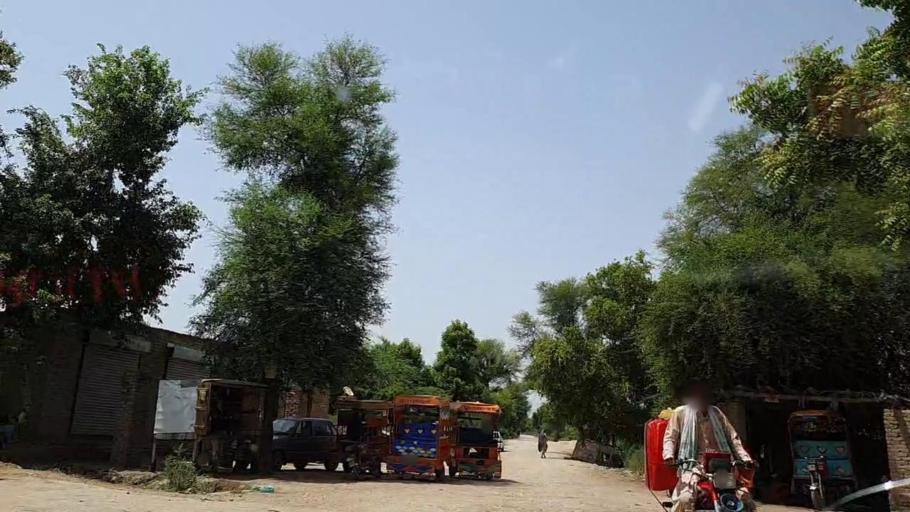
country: PK
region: Sindh
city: Tharu Shah
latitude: 26.8937
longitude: 68.0102
